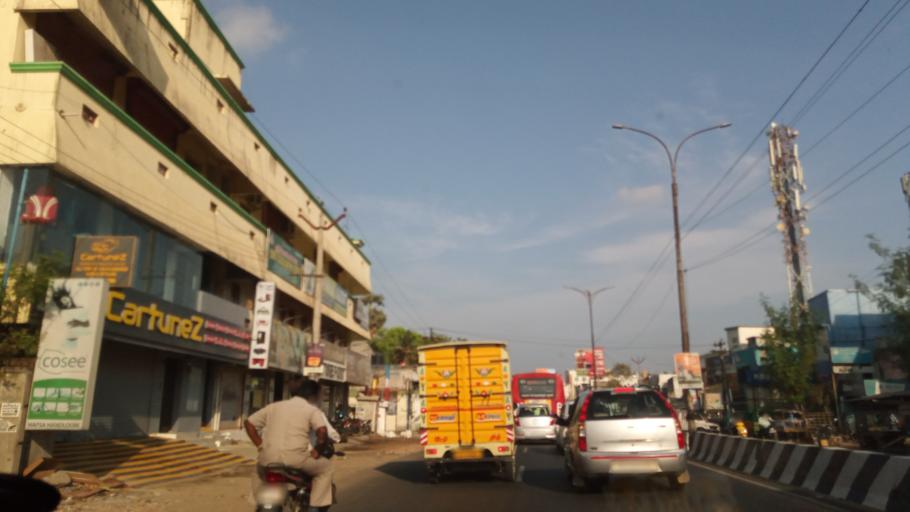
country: IN
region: Tamil Nadu
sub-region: Kancheepuram
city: Poonamalle
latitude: 13.0416
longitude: 80.1263
